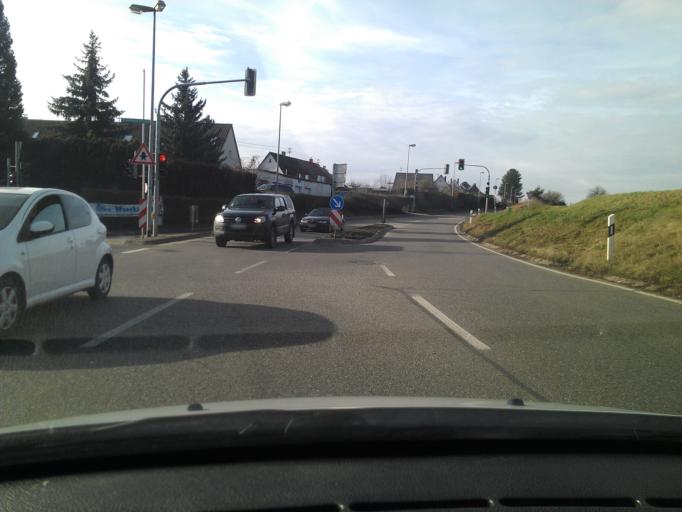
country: DE
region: Baden-Wuerttemberg
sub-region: Regierungsbezirk Stuttgart
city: Neuhausen auf den Fildern
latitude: 48.6902
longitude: 9.2799
